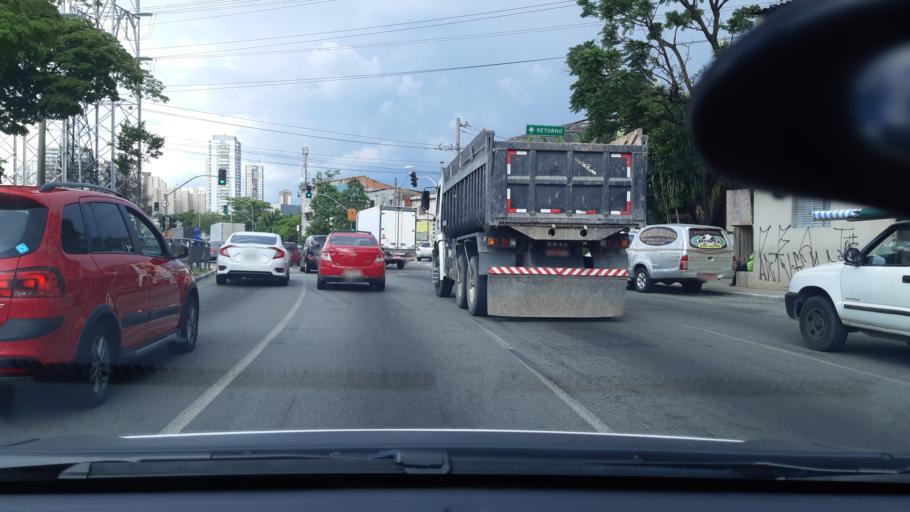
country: BR
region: Sao Paulo
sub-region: Sao Caetano Do Sul
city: Sao Caetano do Sul
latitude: -23.5864
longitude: -46.5893
